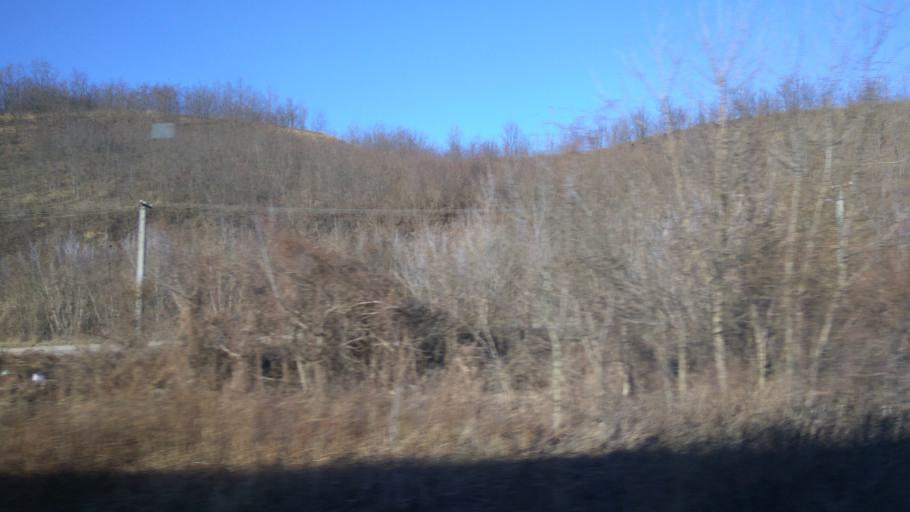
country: HU
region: Pest
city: Pecel
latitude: 47.4948
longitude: 19.3508
